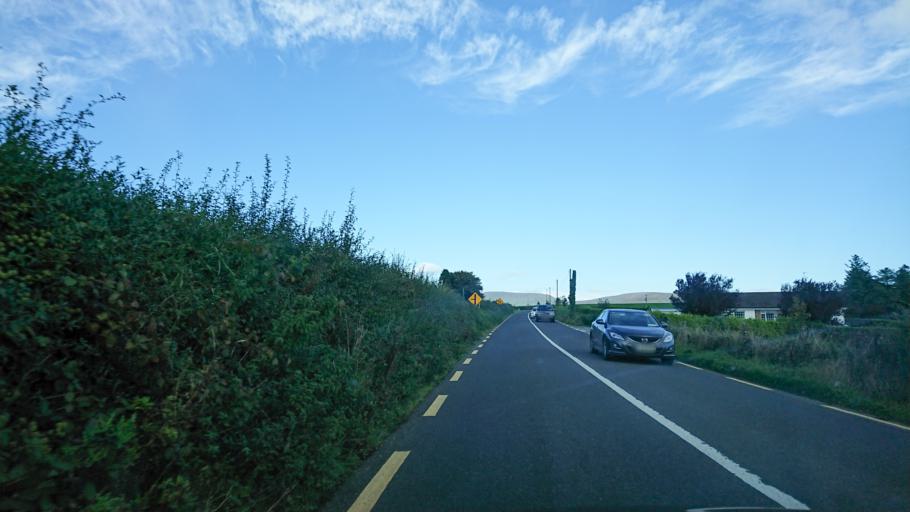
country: IE
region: Munster
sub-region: Waterford
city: Dungarvan
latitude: 52.1366
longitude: -7.6954
